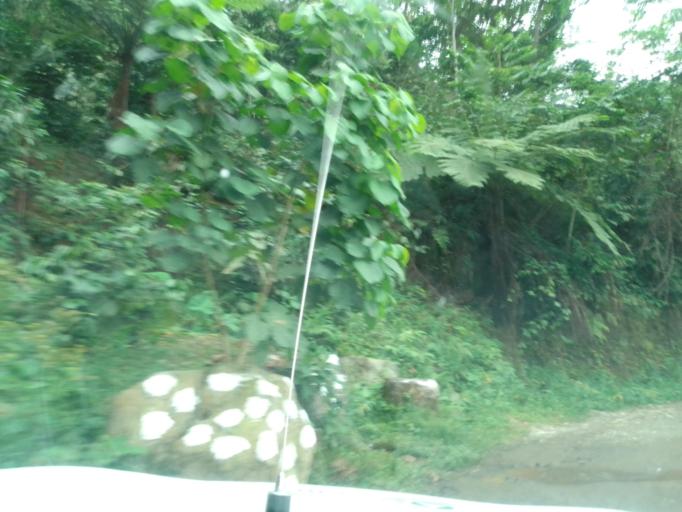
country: MX
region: Chiapas
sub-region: Union Juarez
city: Santo Domingo
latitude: 15.0639
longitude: -92.1249
